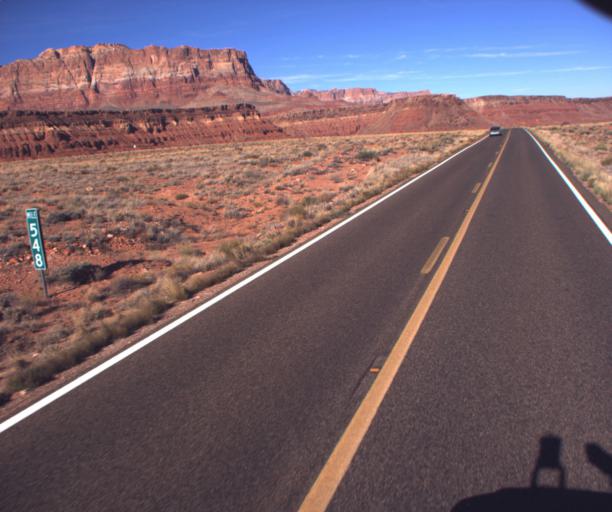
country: US
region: Arizona
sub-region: Coconino County
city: Page
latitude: 36.7309
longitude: -111.7596
